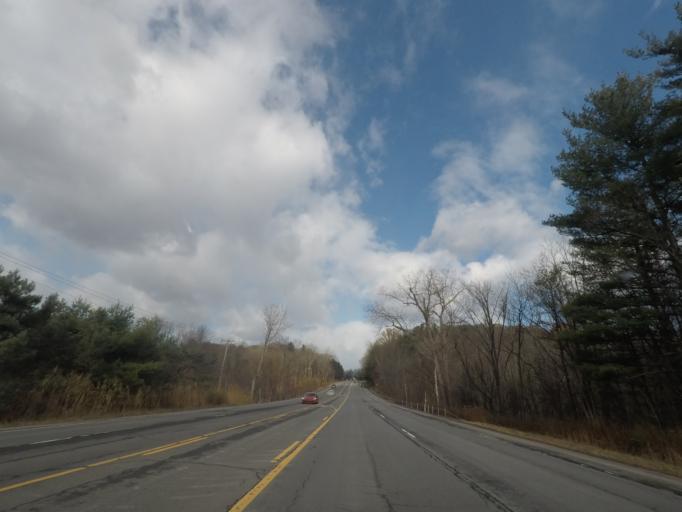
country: US
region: New York
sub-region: Saratoga County
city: Ballston Spa
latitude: 43.0060
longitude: -73.7902
